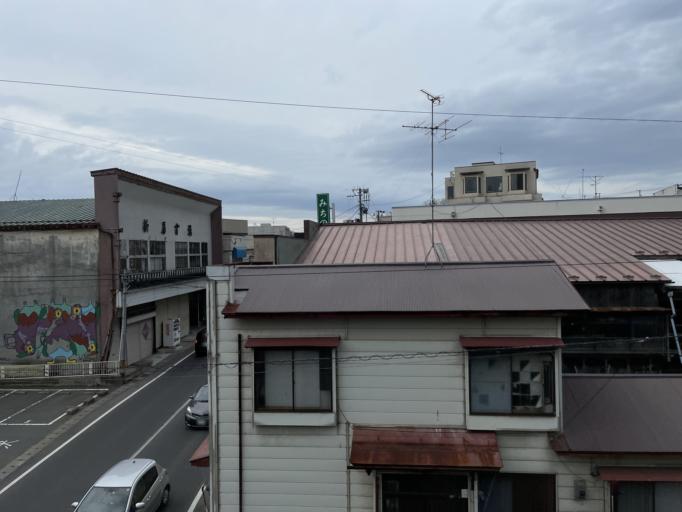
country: JP
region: Aomori
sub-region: Hachinohe Shi
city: Uchimaru
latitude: 40.5222
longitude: 141.5248
